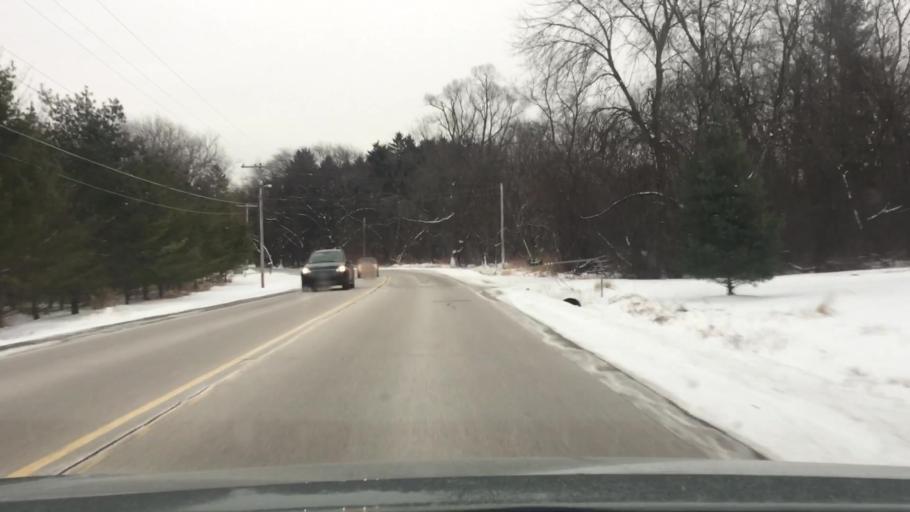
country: US
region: Wisconsin
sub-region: Waukesha County
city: Hartland
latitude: 43.0489
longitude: -88.3158
